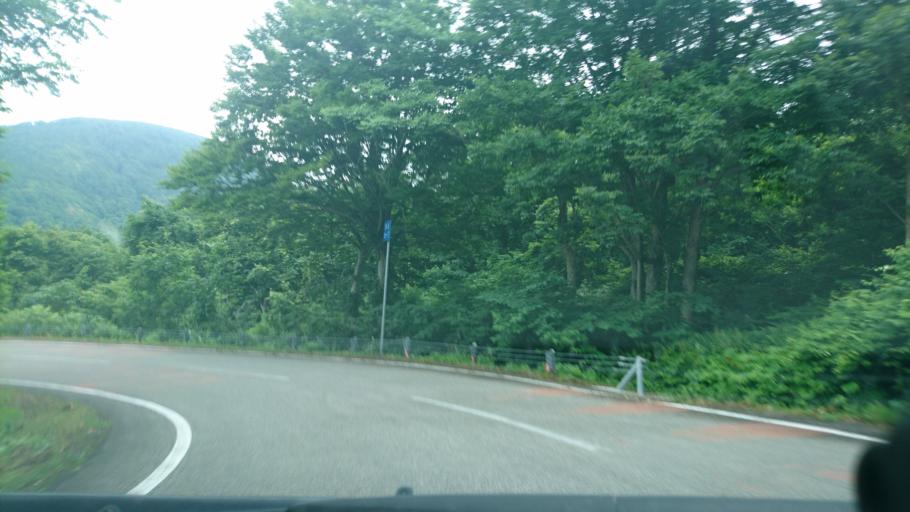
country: JP
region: Akita
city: Yuzawa
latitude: 39.1576
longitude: 140.7510
